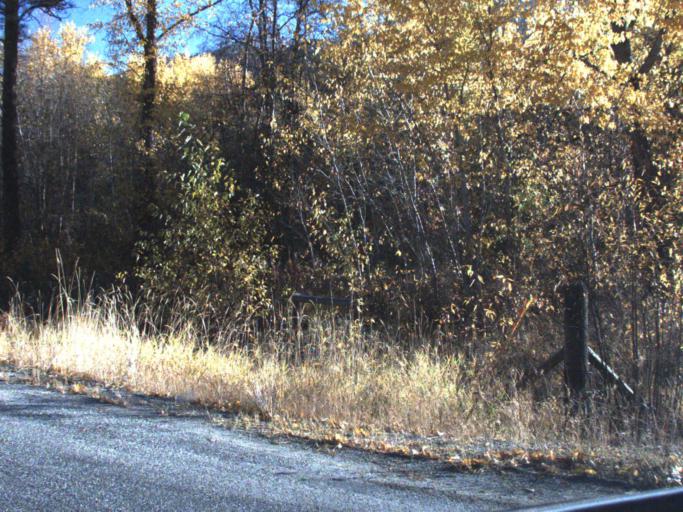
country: US
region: Washington
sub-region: Okanogan County
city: Coulee Dam
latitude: 48.2300
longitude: -118.7021
